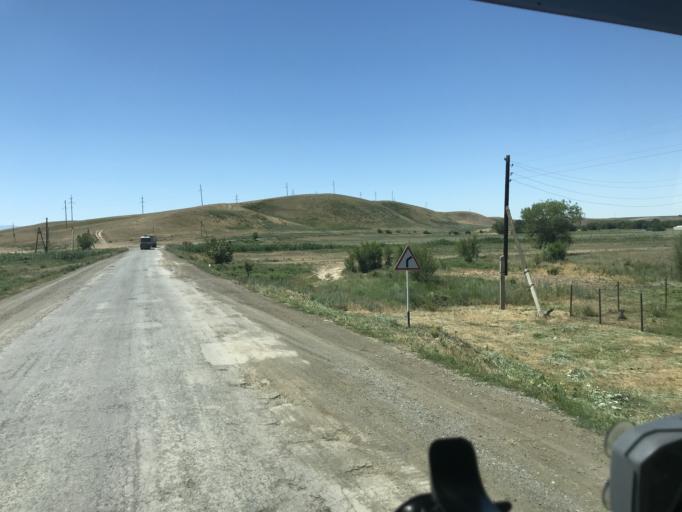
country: KZ
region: Almaty Oblysy
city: Sarkand
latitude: 45.6393
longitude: 80.2255
